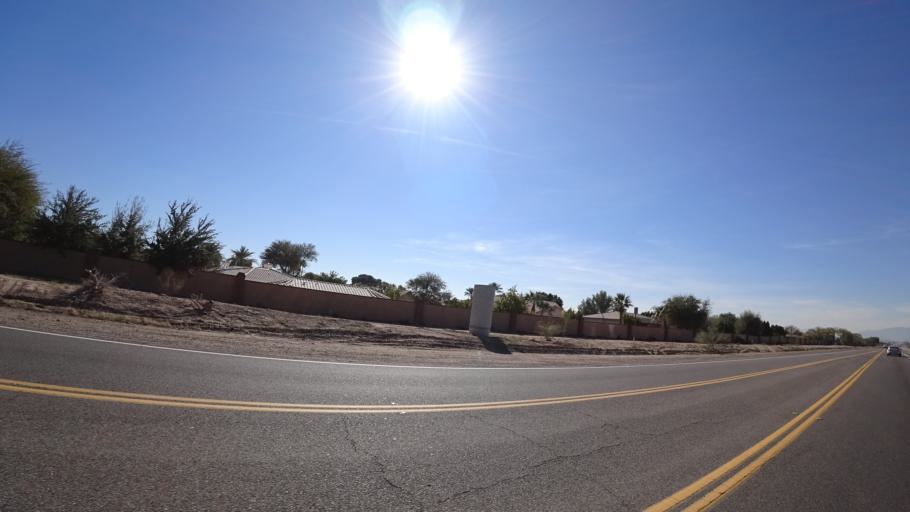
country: US
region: Arizona
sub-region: Maricopa County
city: Litchfield Park
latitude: 33.5083
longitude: -112.3619
